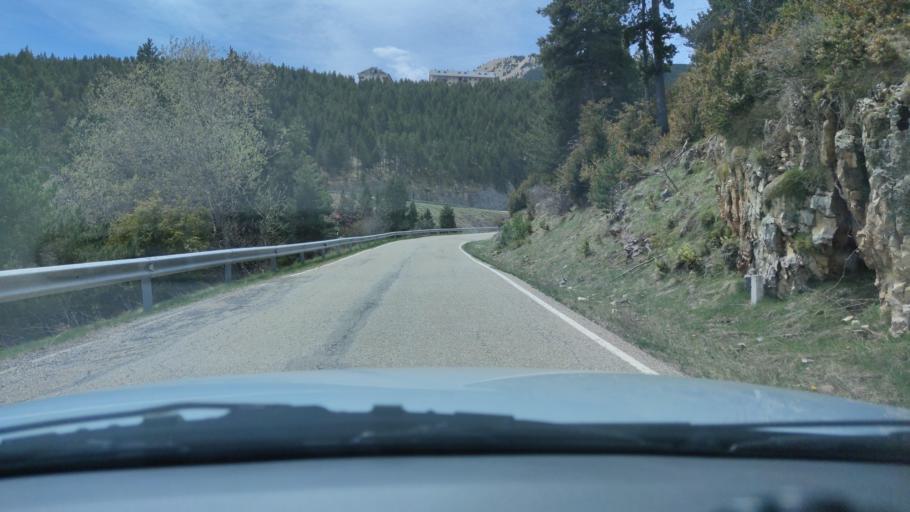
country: ES
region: Catalonia
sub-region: Provincia de Lleida
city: Gosol
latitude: 42.1777
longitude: 1.5590
